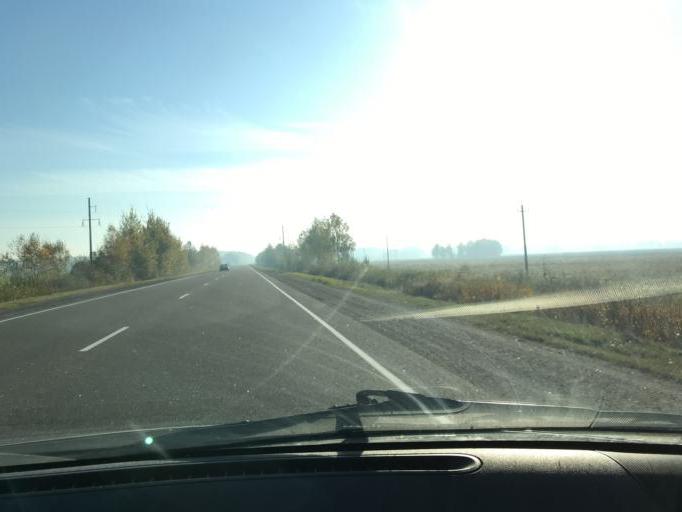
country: BY
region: Brest
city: Horad Luninyets
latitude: 52.3129
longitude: 26.6563
